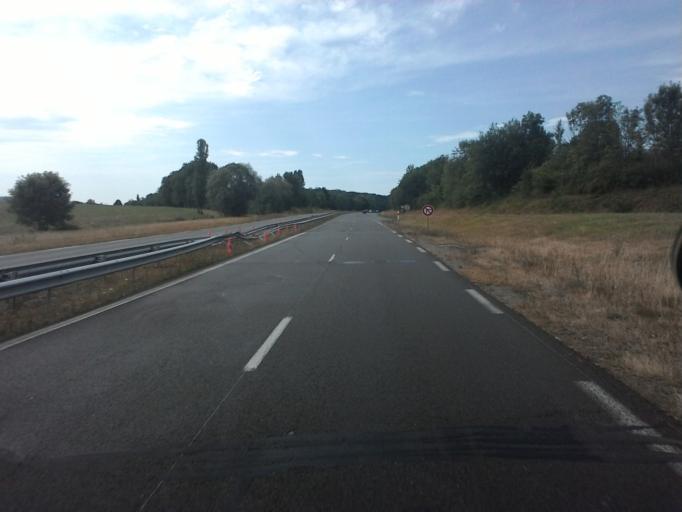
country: FR
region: Franche-Comte
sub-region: Departement du Jura
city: Lons-le-Saunier
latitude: 46.7248
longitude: 5.5574
